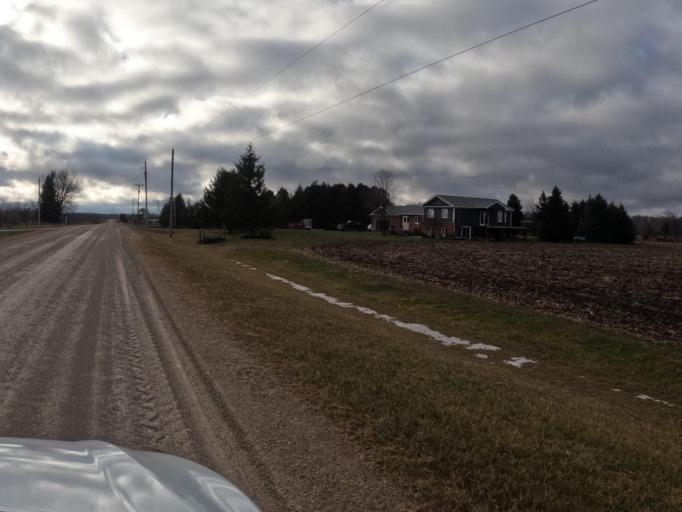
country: CA
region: Ontario
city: Shelburne
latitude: 43.8786
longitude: -80.3574
